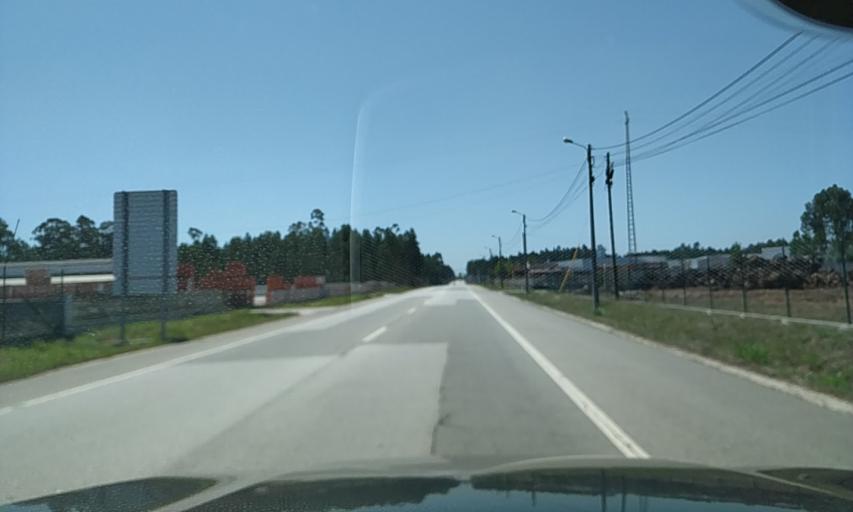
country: PT
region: Aveiro
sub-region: Agueda
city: Aguada de Cima
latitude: 40.4997
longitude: -8.4425
